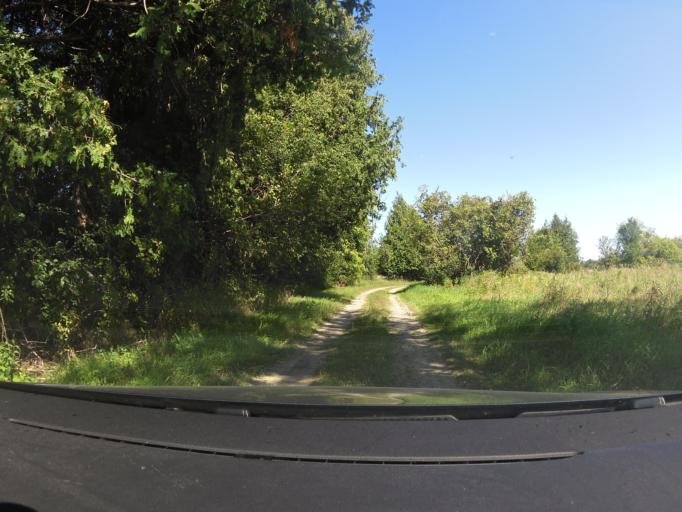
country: CA
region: Ontario
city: Bells Corners
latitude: 45.2869
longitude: -76.0034
